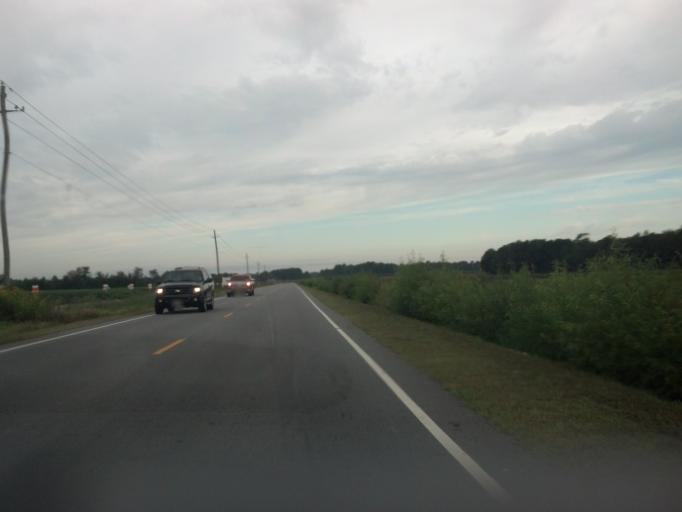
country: US
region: North Carolina
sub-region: Pitt County
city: Ayden
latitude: 35.4763
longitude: -77.4433
